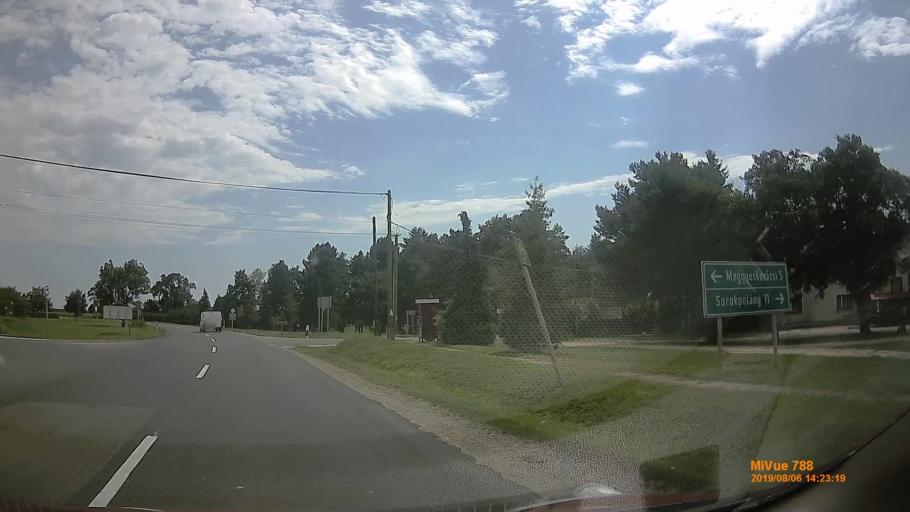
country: HU
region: Vas
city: Vasvar
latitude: 47.1551
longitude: 16.8038
